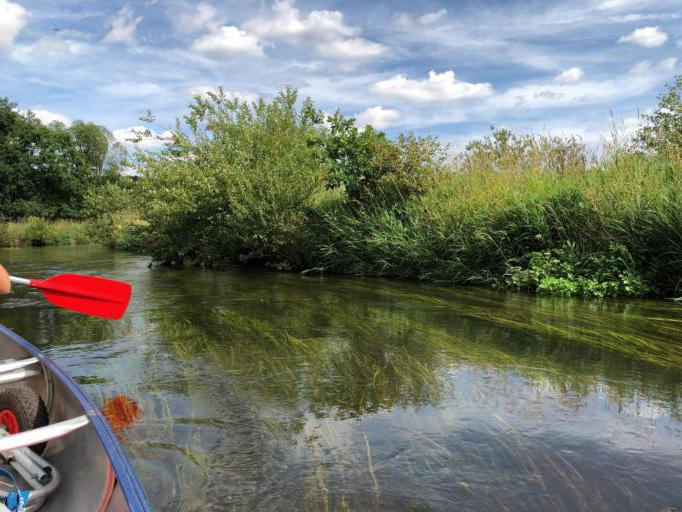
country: DK
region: South Denmark
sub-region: Vejle Kommune
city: Egtved
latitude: 55.6636
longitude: 9.3265
